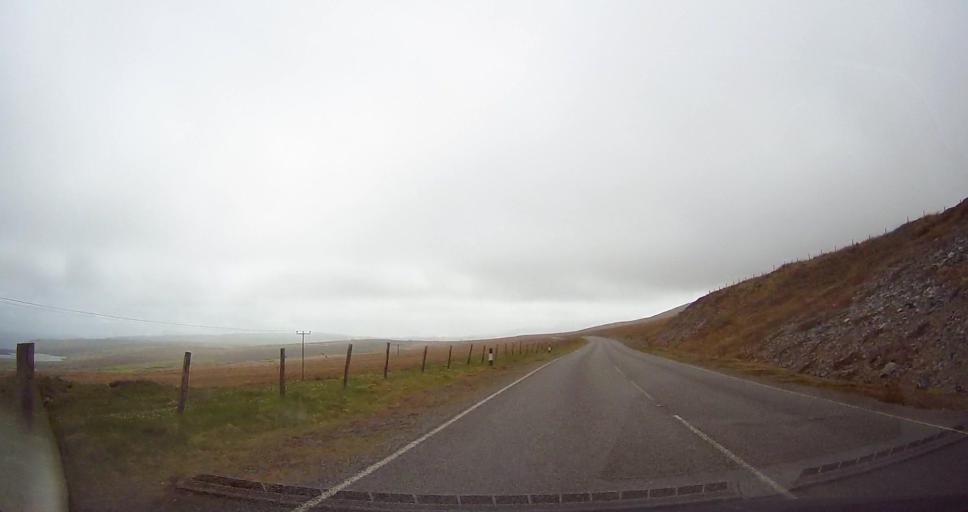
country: GB
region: Scotland
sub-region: Shetland Islands
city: Sandwick
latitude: 59.9557
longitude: -1.2879
